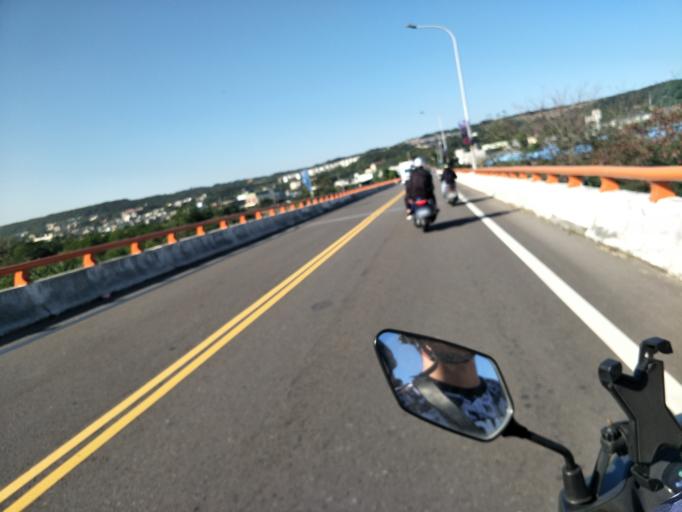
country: TW
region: Taiwan
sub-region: Hsinchu
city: Zhubei
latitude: 24.8365
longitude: 121.0363
